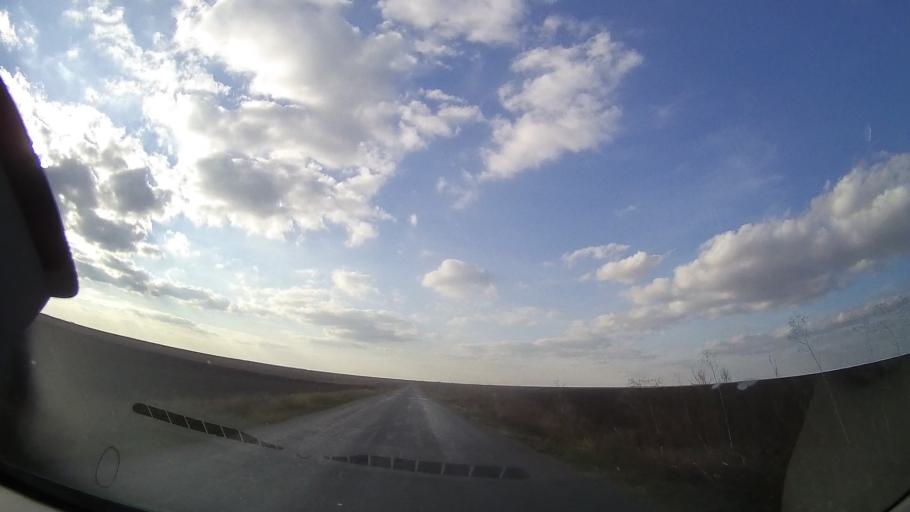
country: RO
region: Constanta
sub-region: Comuna Negru Voda
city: Negru Voda
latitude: 43.8204
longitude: 28.1727
